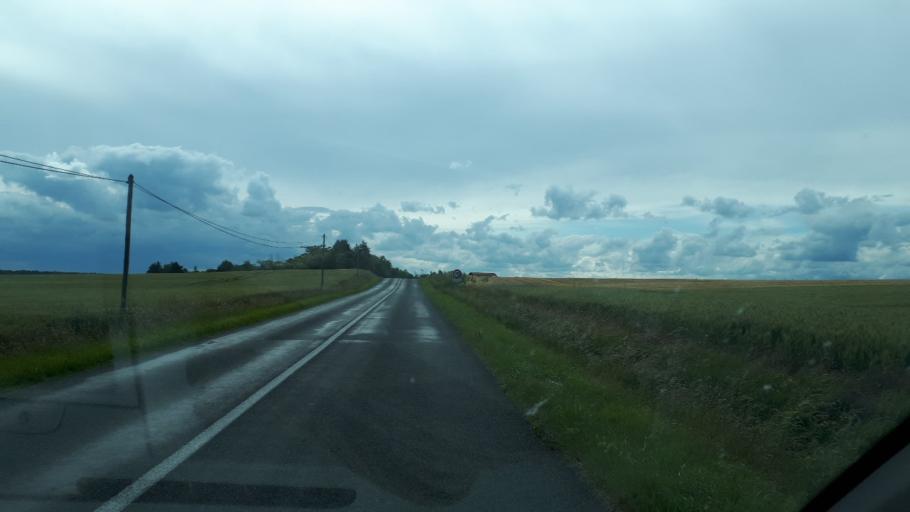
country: FR
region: Centre
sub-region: Departement du Cher
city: Mehun-sur-Yevre
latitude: 47.0815
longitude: 2.2116
